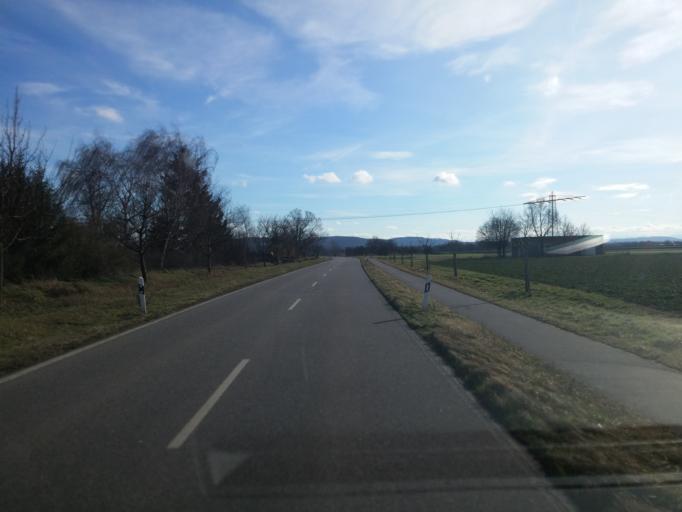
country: DE
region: Baden-Wuerttemberg
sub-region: Karlsruhe Region
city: Karlsdorf-Neuthard
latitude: 49.1086
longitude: 8.5175
